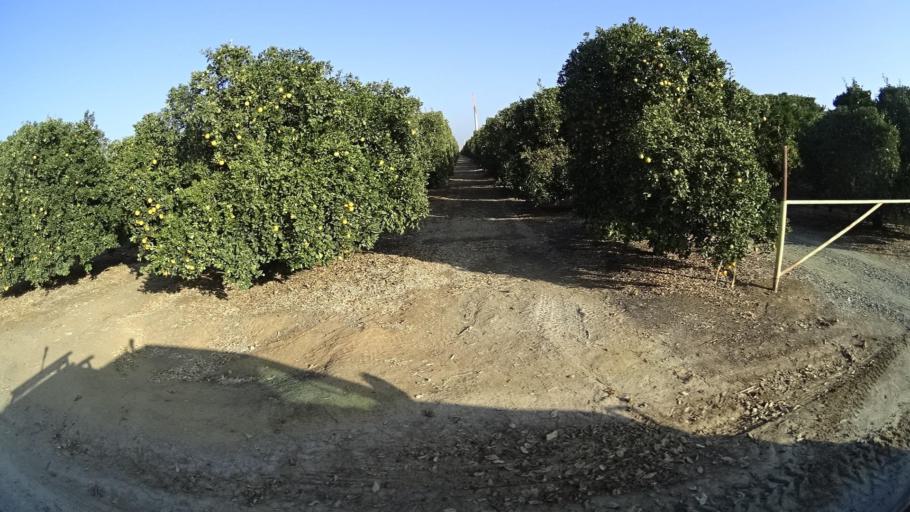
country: US
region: California
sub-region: Tulare County
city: Richgrove
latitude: 35.7763
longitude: -119.0841
